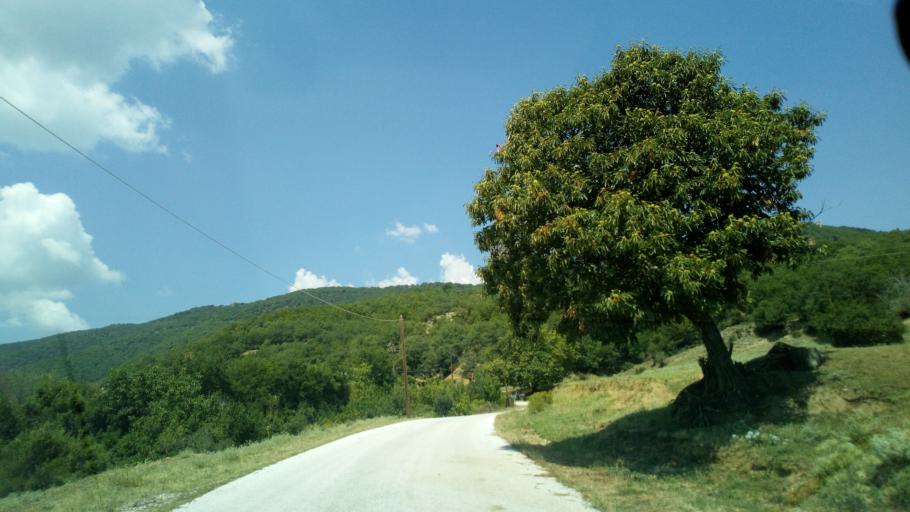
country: GR
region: Central Macedonia
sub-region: Nomos Thessalonikis
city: Sochos
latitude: 40.8170
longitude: 23.3401
